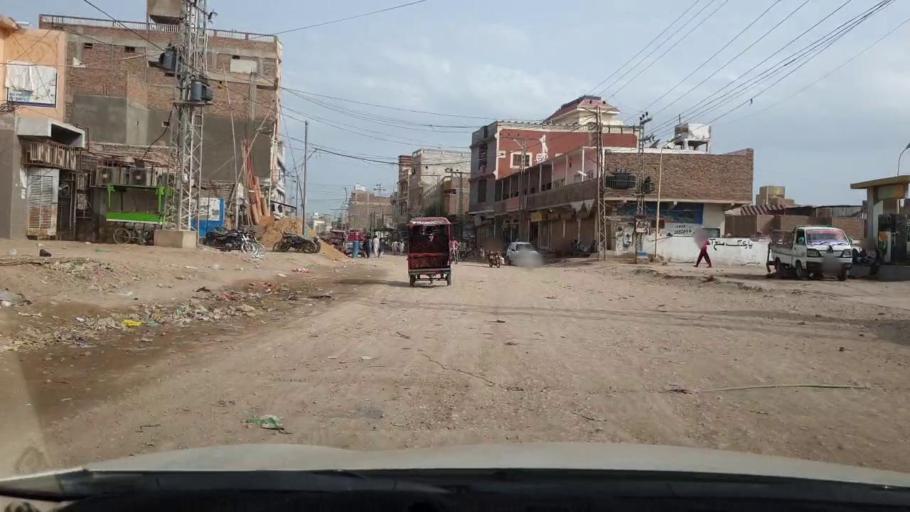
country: PK
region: Sindh
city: Matli
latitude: 25.0408
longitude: 68.6610
